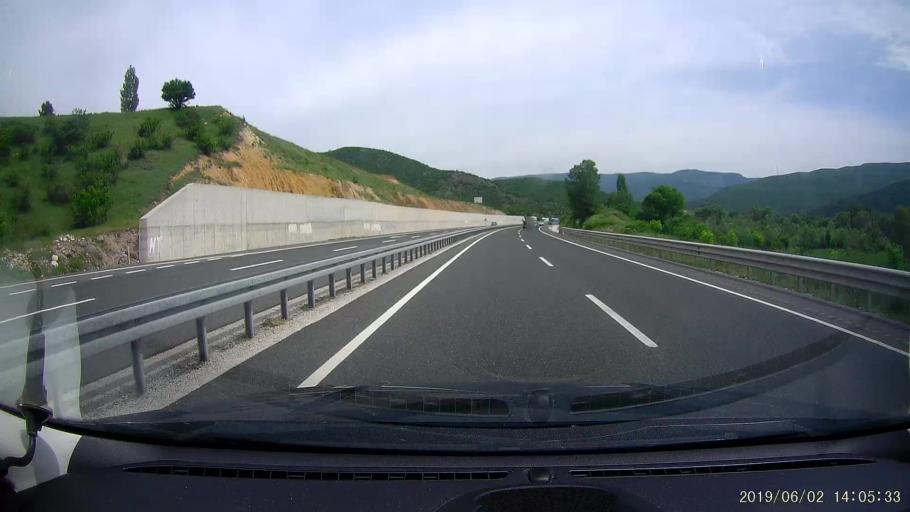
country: TR
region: Cankiri
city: Ilgaz
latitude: 40.9003
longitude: 33.6708
